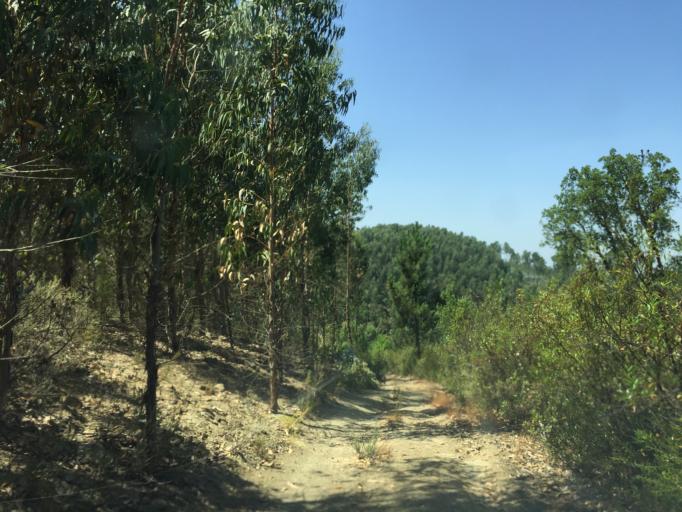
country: PT
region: Santarem
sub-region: Ferreira do Zezere
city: Ferreira do Zezere
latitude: 39.6514
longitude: -8.3170
